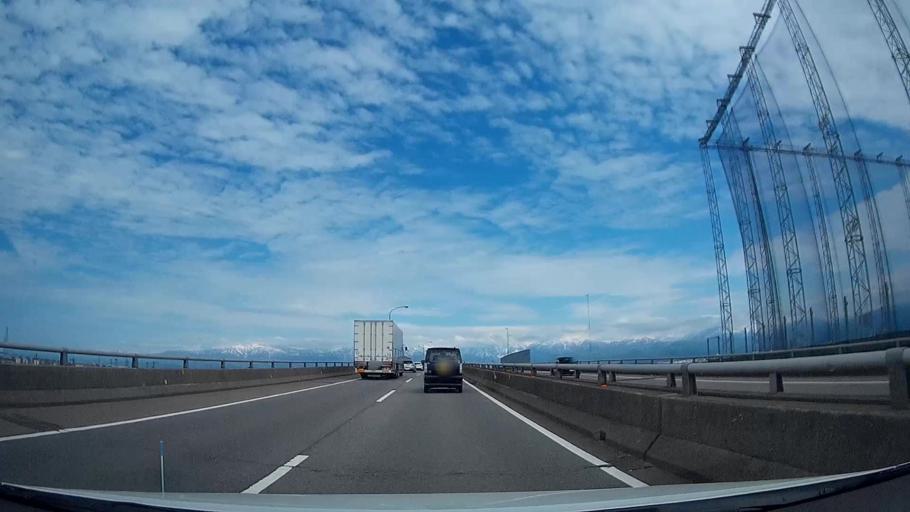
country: JP
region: Toyama
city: Toyama-shi
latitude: 36.7237
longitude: 137.2407
